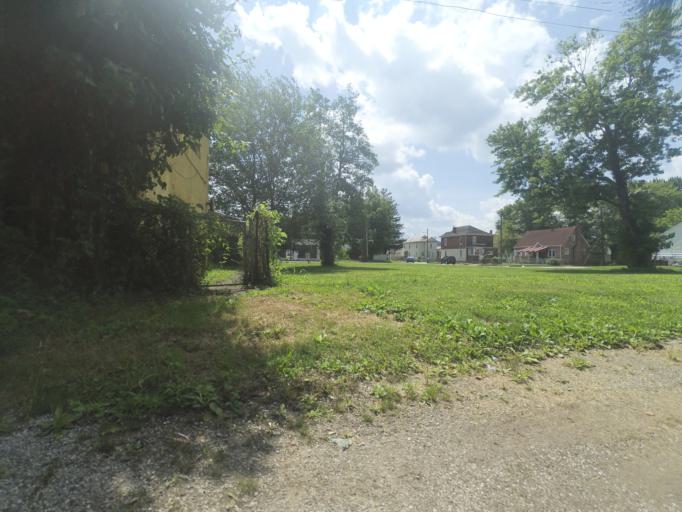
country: US
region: West Virginia
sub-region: Cabell County
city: Huntington
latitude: 38.4136
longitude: -82.4243
